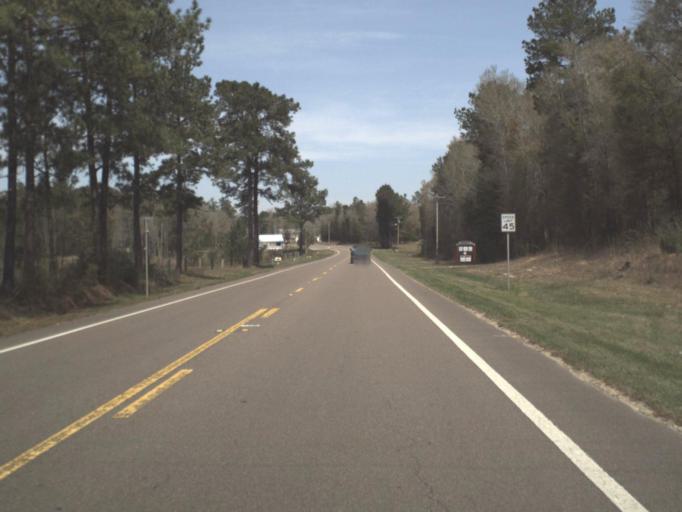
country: US
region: Florida
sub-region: Walton County
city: DeFuniak Springs
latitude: 30.7037
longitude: -85.9344
